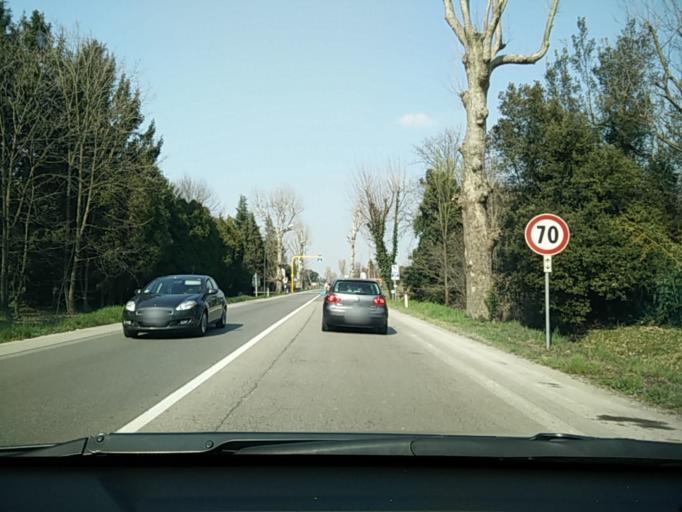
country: IT
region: Veneto
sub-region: Provincia di Treviso
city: Frescada
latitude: 45.6298
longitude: 12.2397
